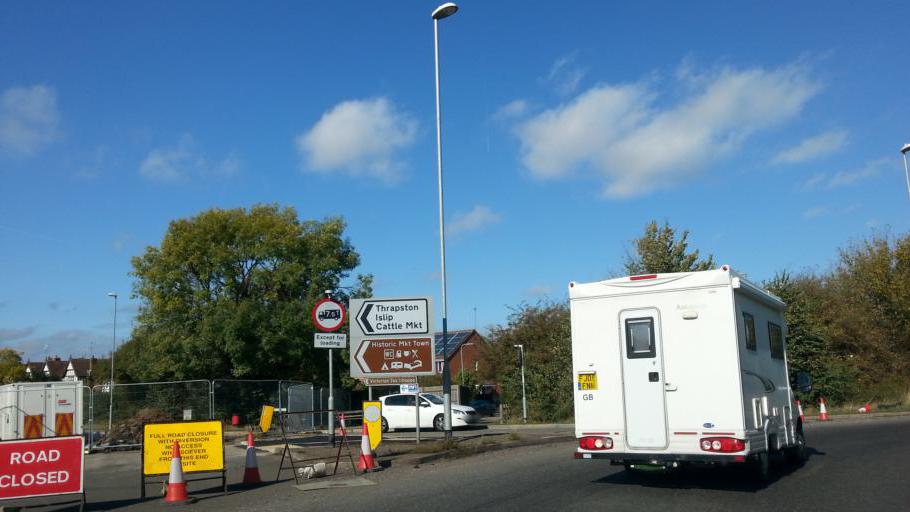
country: GB
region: England
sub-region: Northamptonshire
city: Thrapston
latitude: 52.3944
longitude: -0.5234
